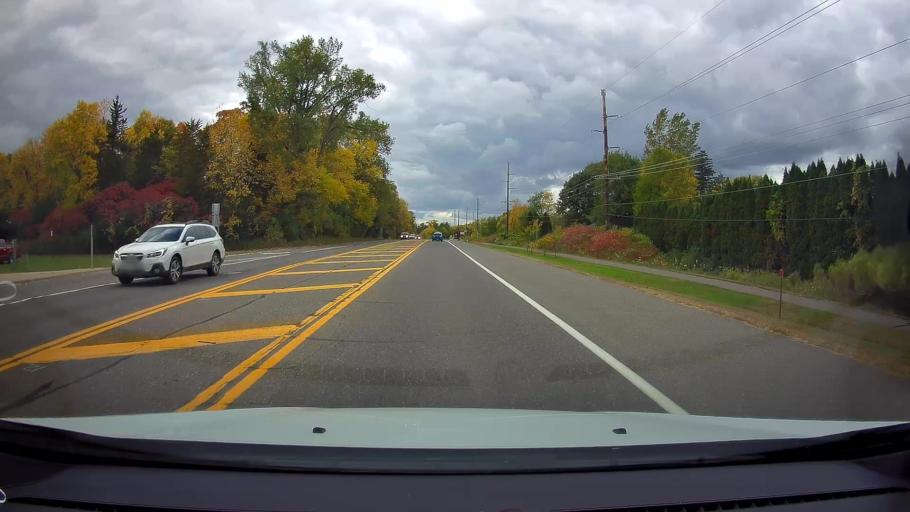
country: US
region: Minnesota
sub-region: Chisago County
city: Center City
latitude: 45.3900
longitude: -92.8199
